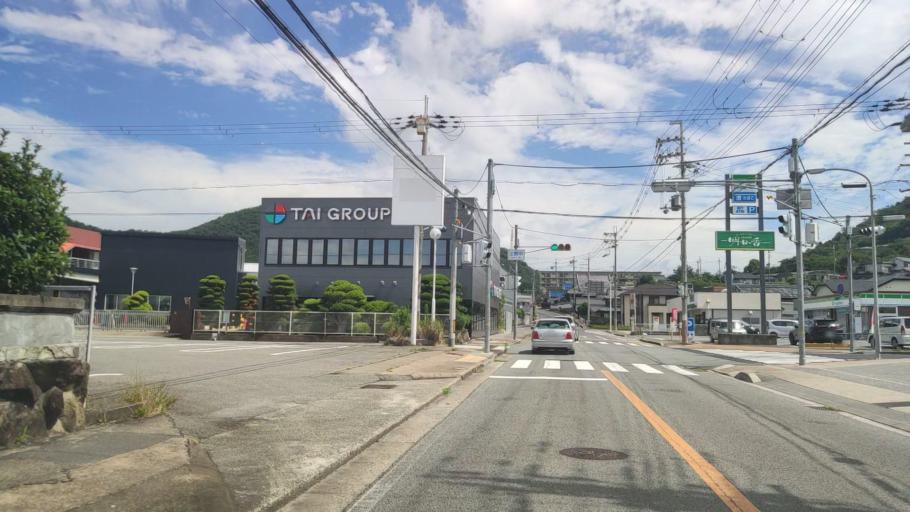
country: JP
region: Hyogo
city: Nishiwaki
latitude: 34.9871
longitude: 134.9786
